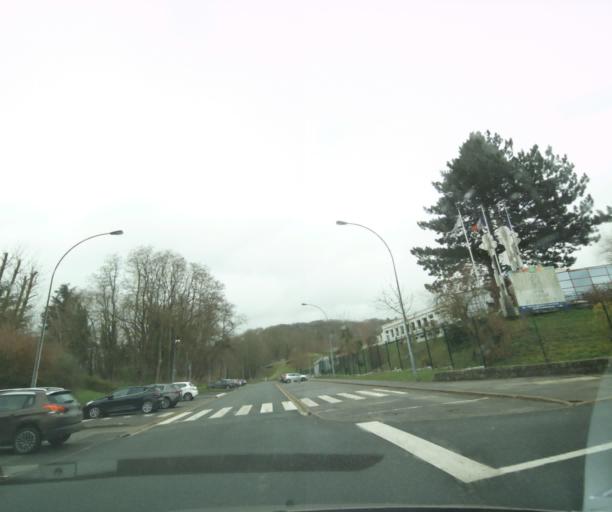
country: FR
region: Picardie
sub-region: Departement de l'Oise
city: Noyon
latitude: 49.5843
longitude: 3.0153
